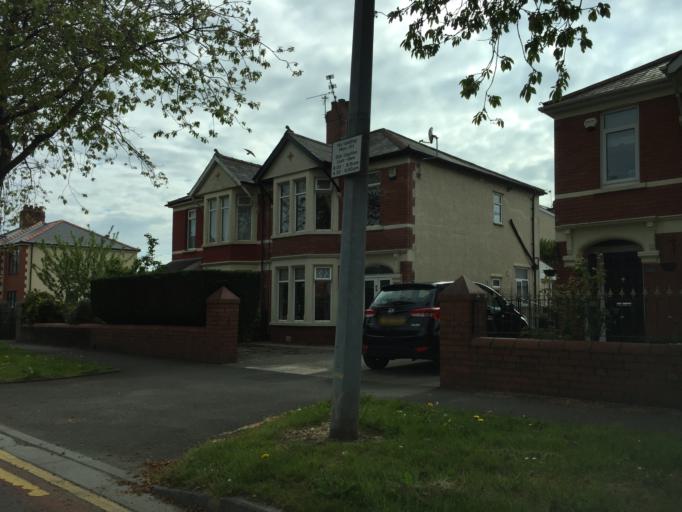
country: GB
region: Wales
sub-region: Cardiff
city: Cardiff
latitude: 51.5231
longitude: -3.2022
